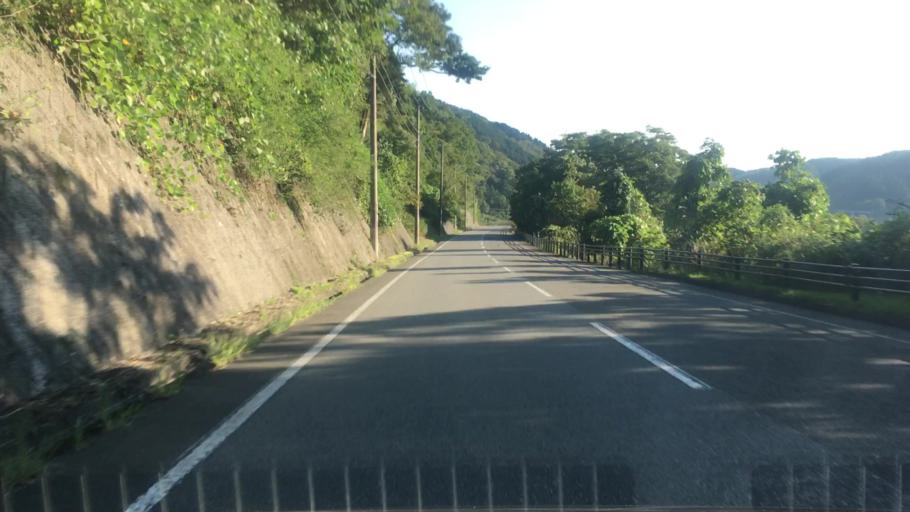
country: JP
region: Hyogo
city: Toyooka
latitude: 35.6014
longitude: 134.8060
